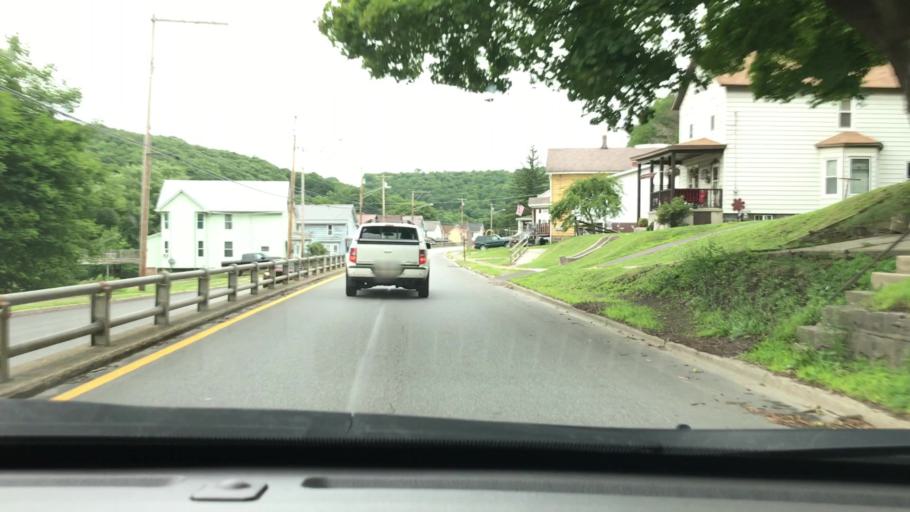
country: US
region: Pennsylvania
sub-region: Elk County
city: Ridgway
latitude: 41.4331
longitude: -78.7345
